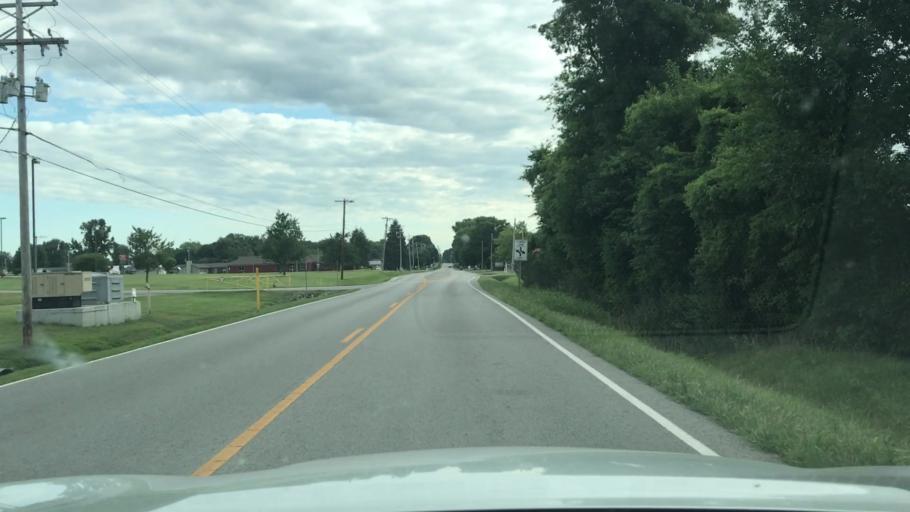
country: US
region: Kentucky
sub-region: Todd County
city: Elkton
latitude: 36.7960
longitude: -87.1609
